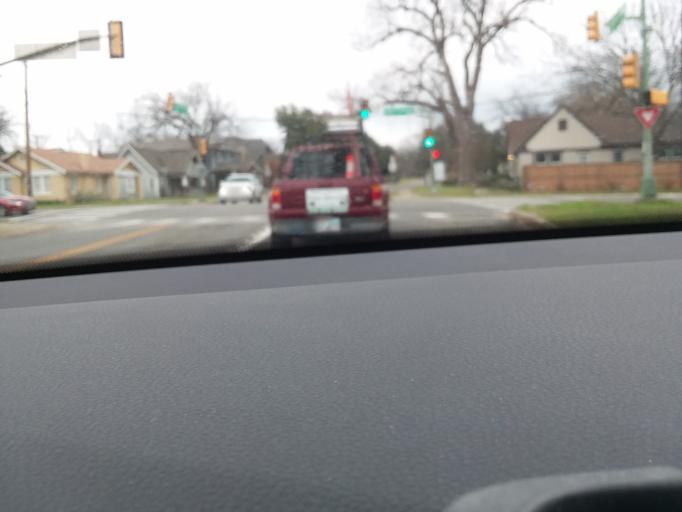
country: US
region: Texas
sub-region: Dallas County
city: Highland Park
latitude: 32.8160
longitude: -96.7618
